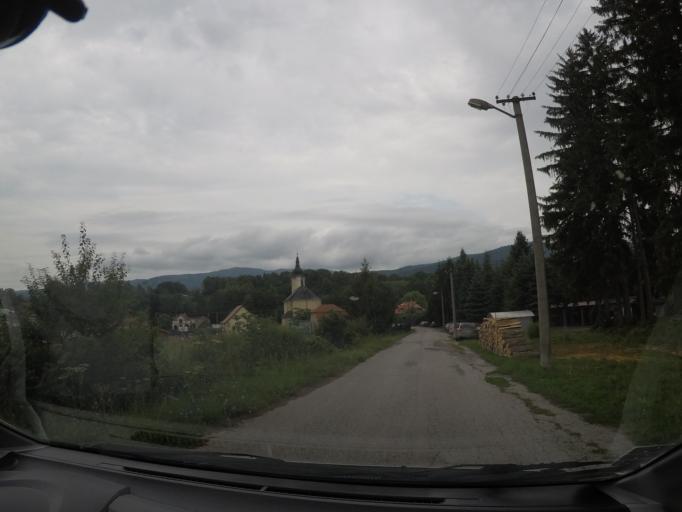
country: SK
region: Nitriansky
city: Bojnice
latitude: 48.8871
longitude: 18.6244
